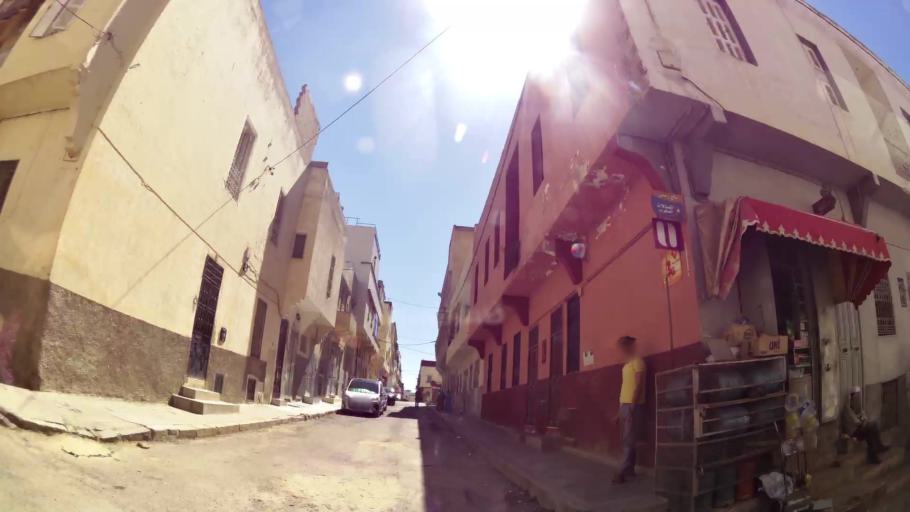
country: MA
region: Meknes-Tafilalet
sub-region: Meknes
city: Meknes
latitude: 33.8883
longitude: -5.5699
